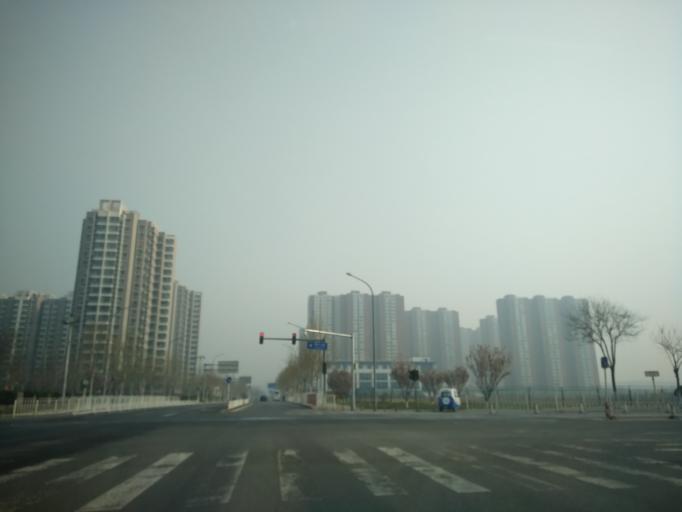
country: CN
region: Beijing
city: Yinghai
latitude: 39.7531
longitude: 116.4941
